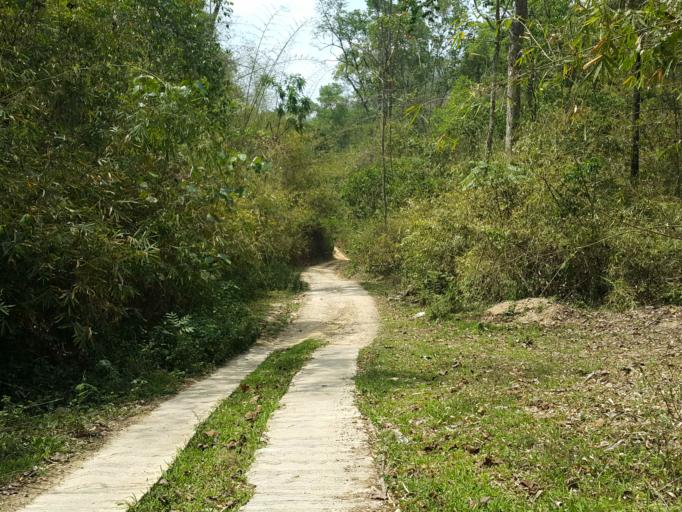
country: TH
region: Chiang Mai
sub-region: Amphoe Chiang Dao
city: Chiang Dao
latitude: 19.2991
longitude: 98.7507
